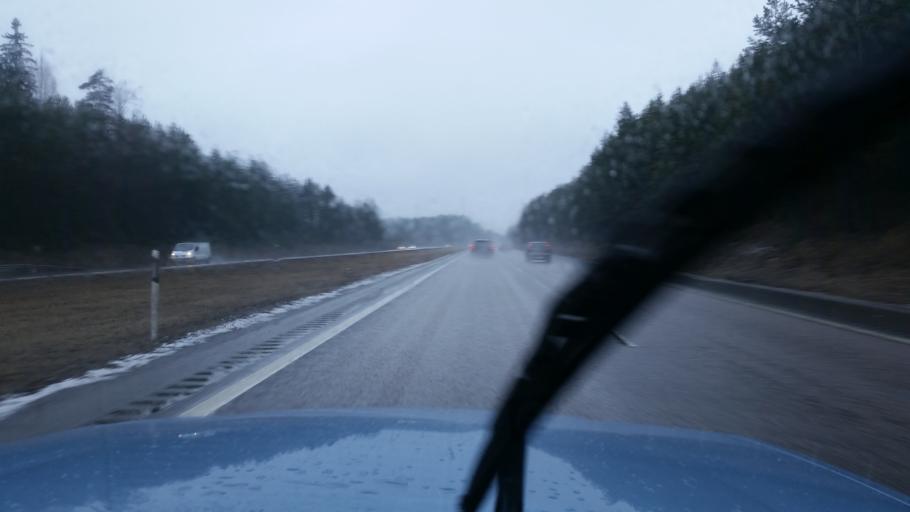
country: FI
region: Haeme
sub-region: Riihimaeki
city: Riihimaeki
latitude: 60.6760
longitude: 24.7682
